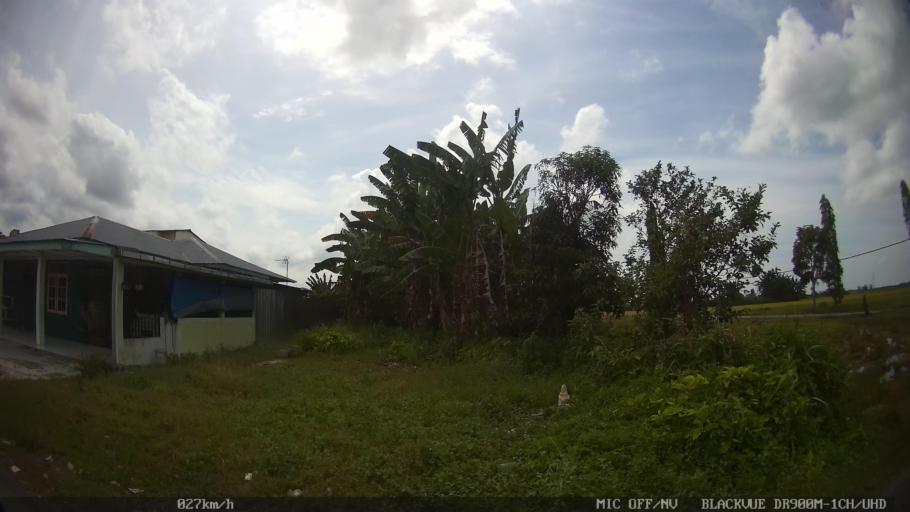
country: ID
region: North Sumatra
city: Percut
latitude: 3.5718
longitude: 98.8502
